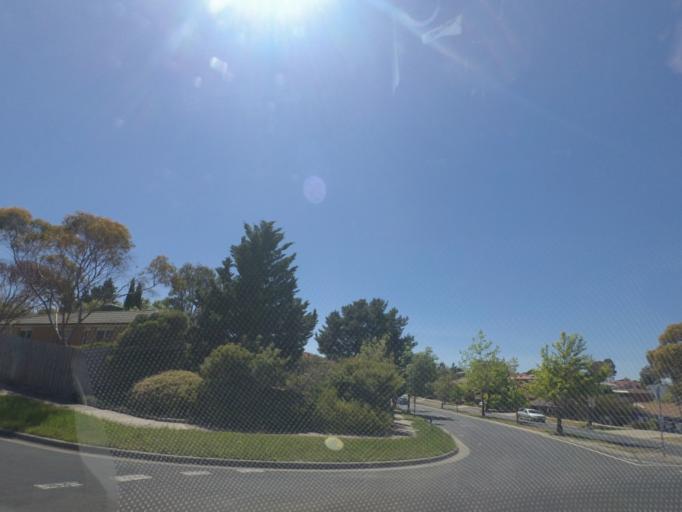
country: AU
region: Victoria
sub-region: Hume
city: Sunbury
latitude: -37.5634
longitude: 144.7052
